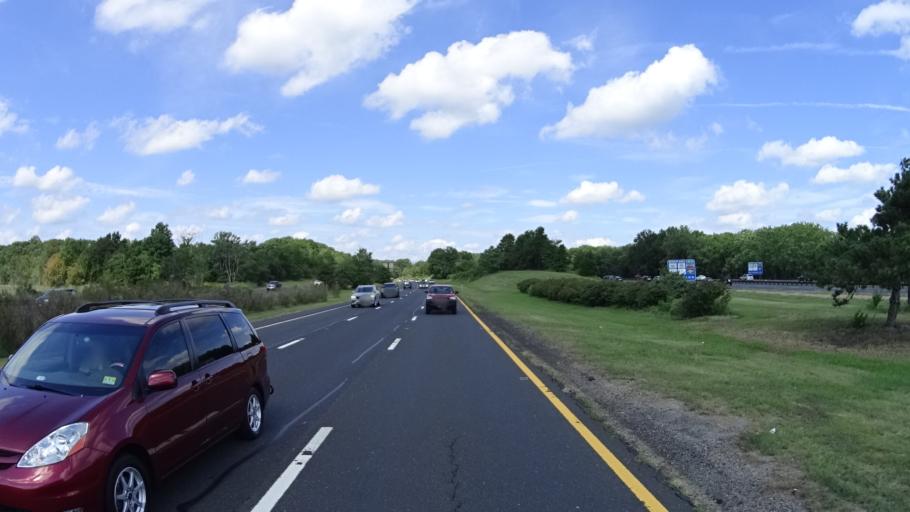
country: US
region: New Jersey
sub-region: Monmouth County
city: Matawan
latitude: 40.4263
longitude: -74.2233
